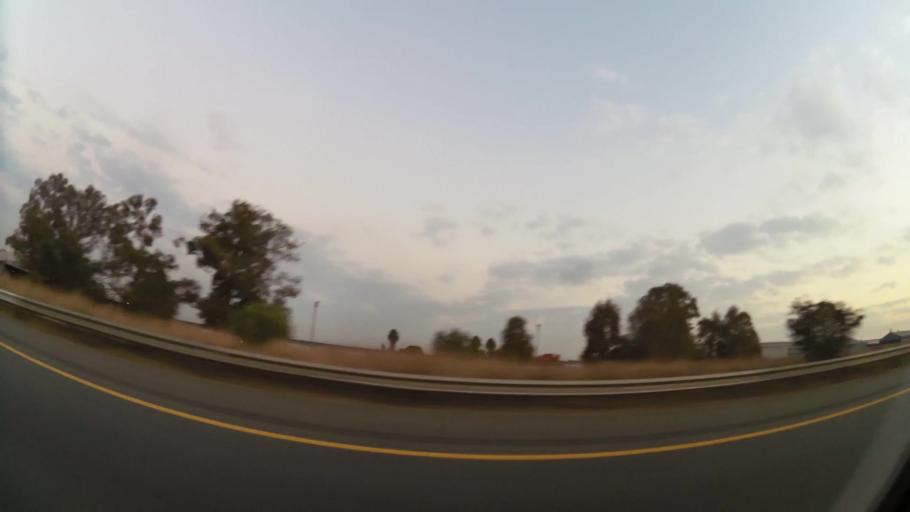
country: ZA
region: Gauteng
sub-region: Ekurhuleni Metropolitan Municipality
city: Germiston
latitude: -26.2579
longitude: 28.1787
